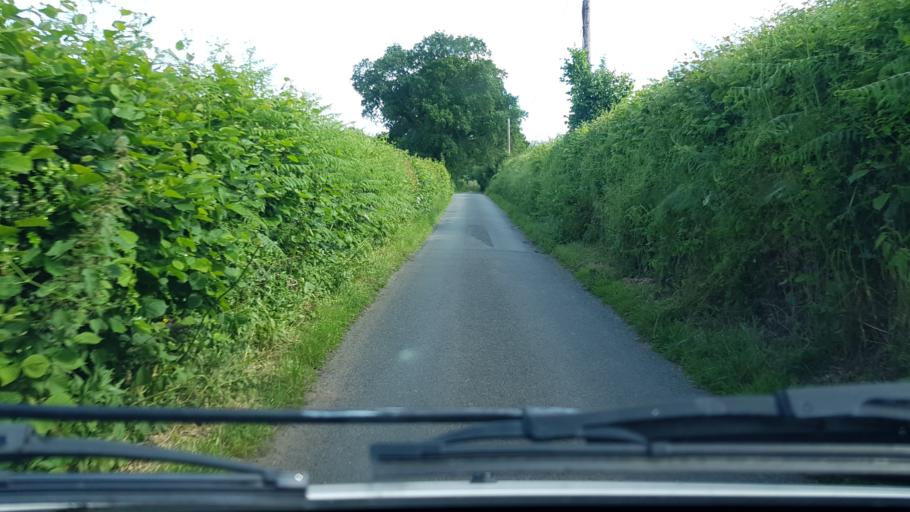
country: GB
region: England
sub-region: Worcestershire
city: Bewdley
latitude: 52.3565
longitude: -2.3273
